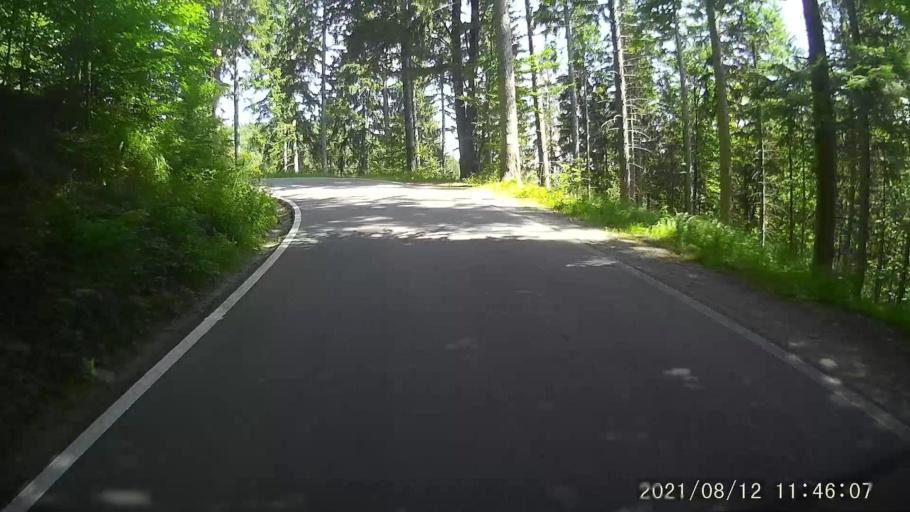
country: PL
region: Lower Silesian Voivodeship
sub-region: Powiat klodzki
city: Stronie Slaskie
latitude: 50.2501
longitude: 16.8441
